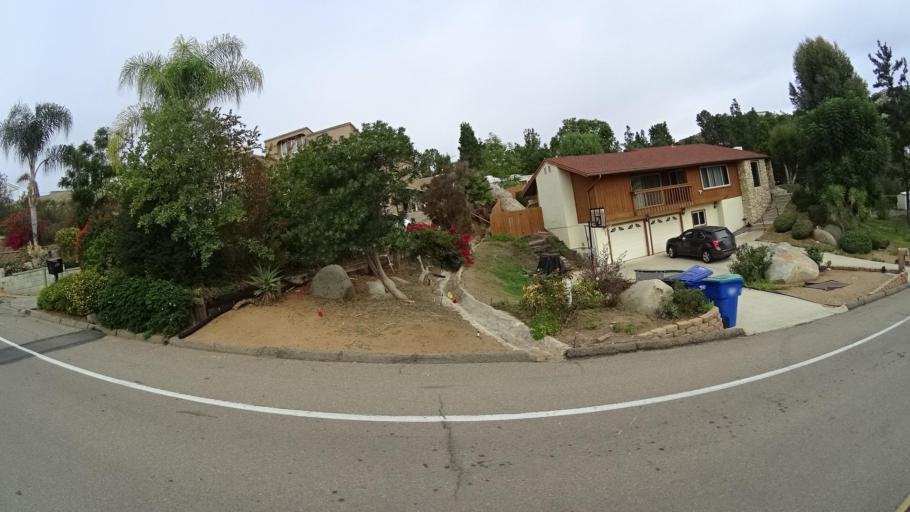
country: US
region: California
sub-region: San Diego County
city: Granite Hills
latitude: 32.7725
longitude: -116.9129
